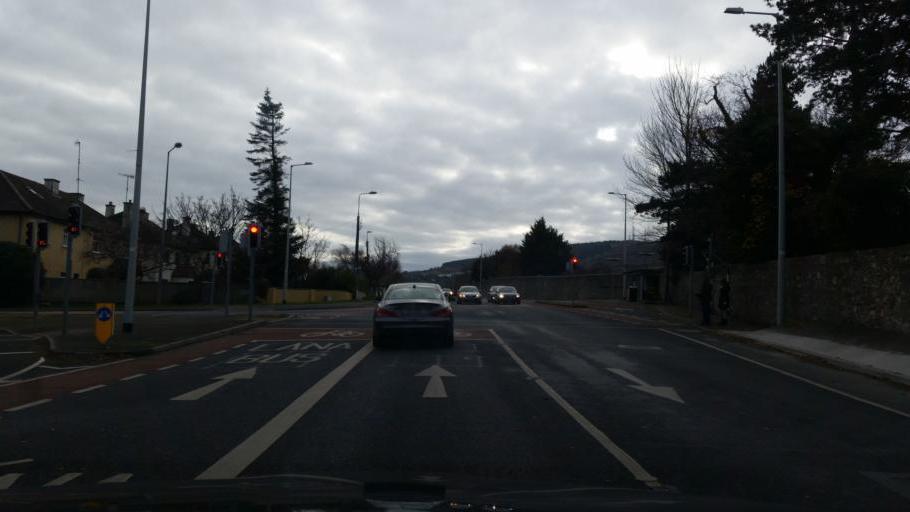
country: IE
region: Leinster
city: Sandyford
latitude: 53.2759
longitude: -6.2295
